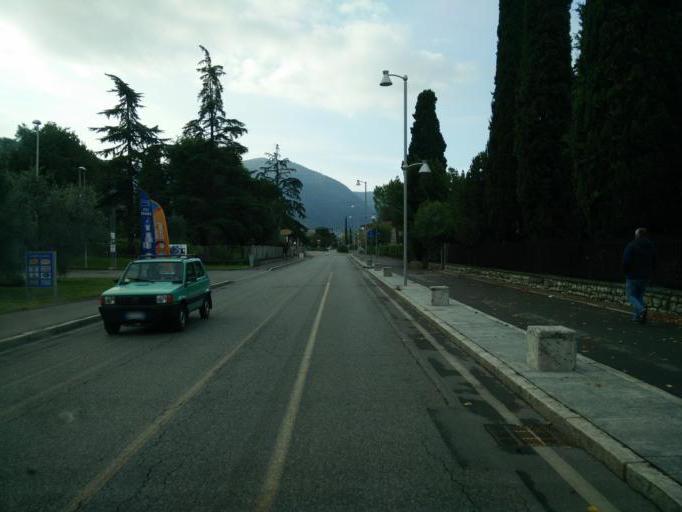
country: IT
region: Lombardy
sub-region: Provincia di Brescia
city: Sale Marasino
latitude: 45.7077
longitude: 10.1095
